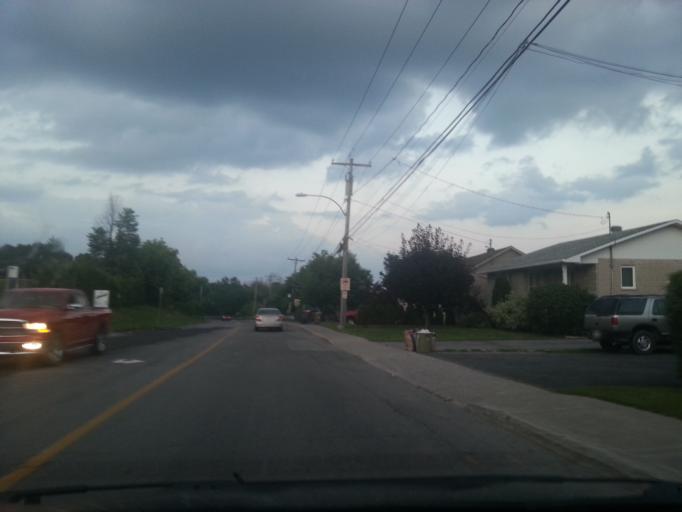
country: CA
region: Quebec
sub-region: Outaouais
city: Gatineau
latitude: 45.4982
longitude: -75.6079
